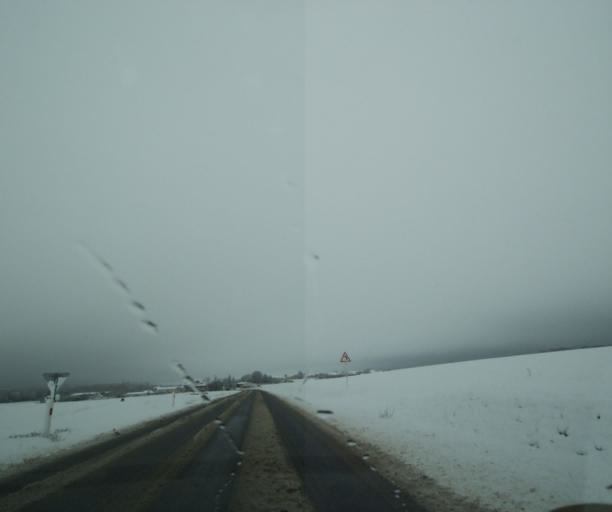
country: FR
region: Champagne-Ardenne
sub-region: Departement de la Haute-Marne
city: Wassy
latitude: 48.5198
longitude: 4.9340
